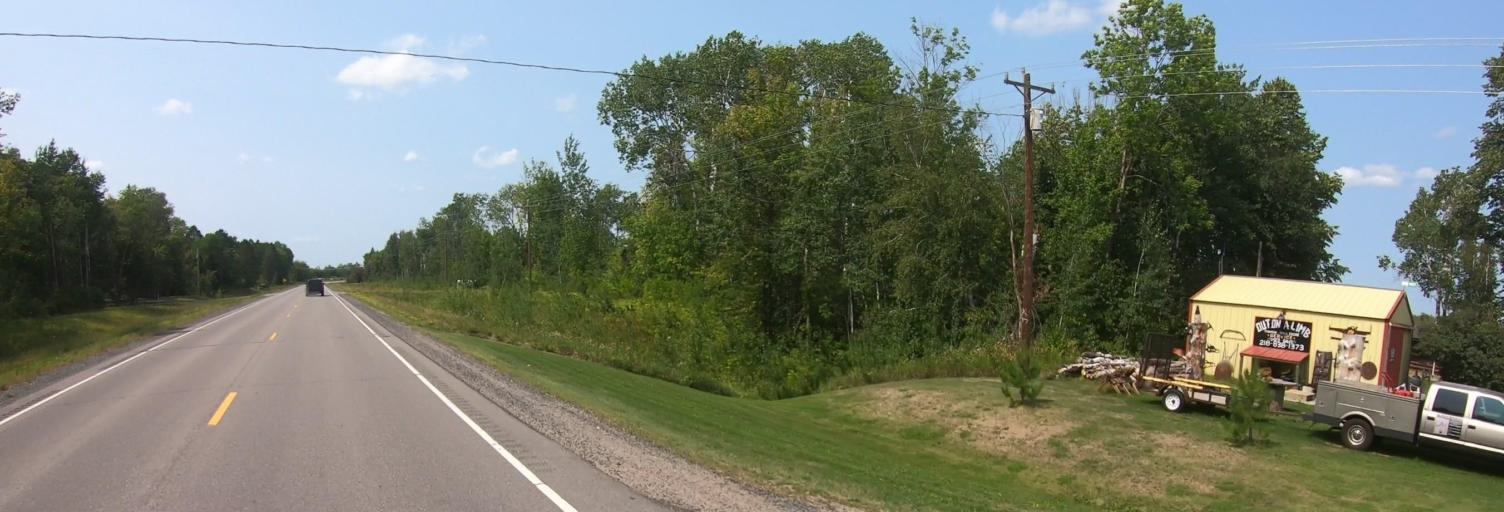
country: US
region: Minnesota
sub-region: Lake of the Woods County
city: Baudette
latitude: 48.6990
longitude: -94.5317
